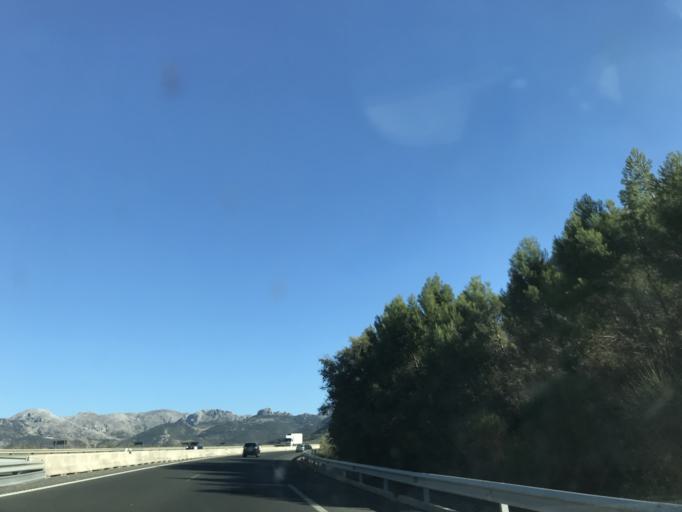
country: ES
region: Andalusia
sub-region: Provincia de Malaga
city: Villanueva del Rosario
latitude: 36.9801
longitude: -4.4476
